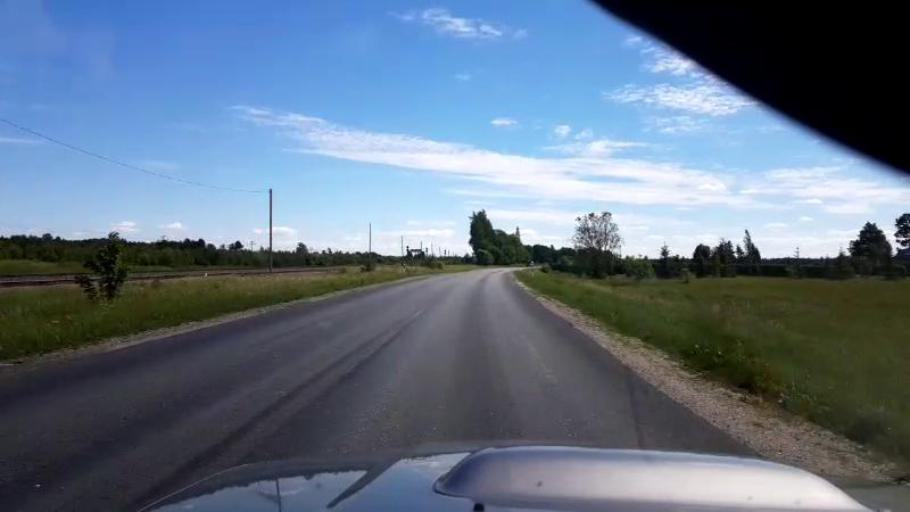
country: EE
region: Laeaene-Virumaa
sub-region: Rakke vald
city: Rakke
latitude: 58.9068
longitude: 26.2800
